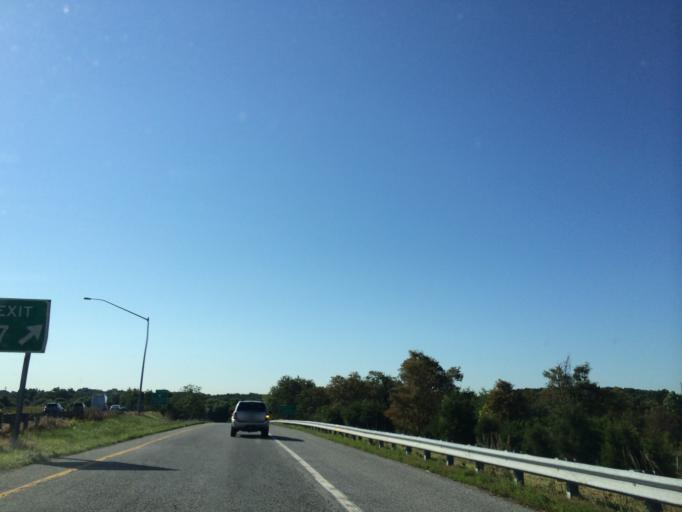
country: US
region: Maryland
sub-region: Howard County
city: Riverside
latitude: 39.1862
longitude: -76.9006
